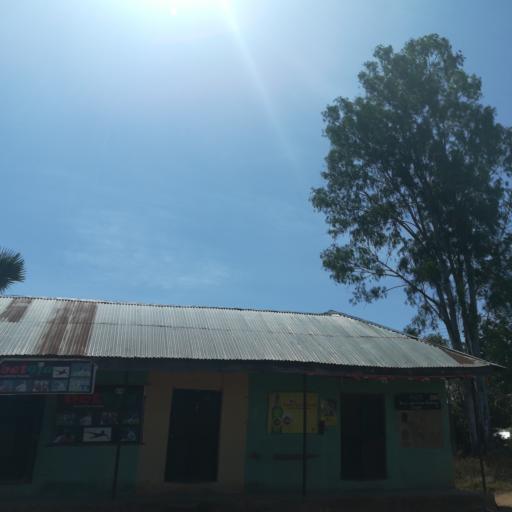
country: NG
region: Plateau
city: Bukuru
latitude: 9.7587
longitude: 8.8654
